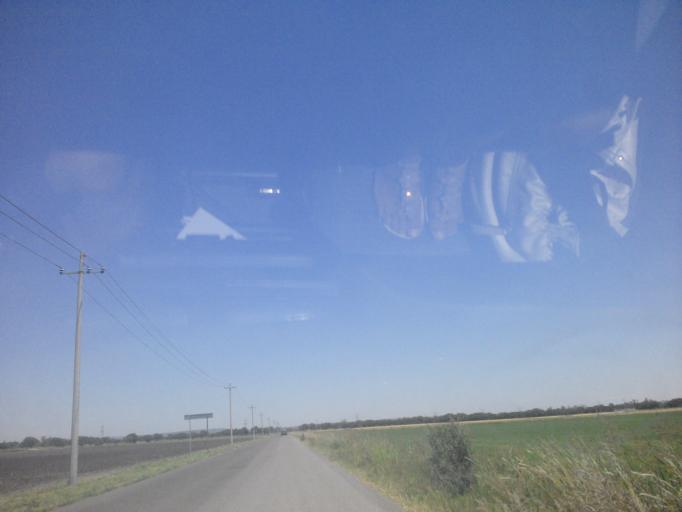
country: MX
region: Guanajuato
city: San Roque
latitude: 20.9553
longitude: -101.8964
